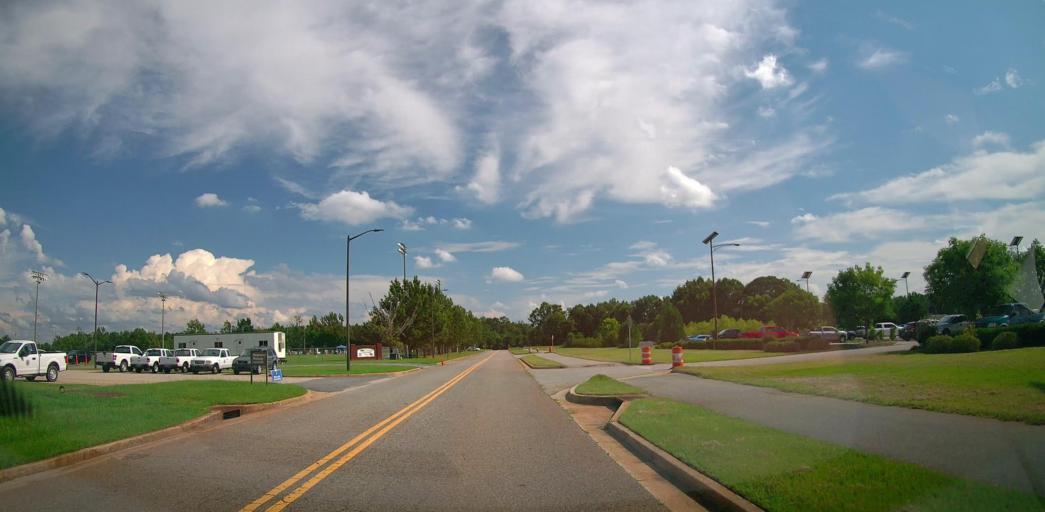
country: US
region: Georgia
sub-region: Houston County
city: Centerville
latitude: 32.5455
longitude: -83.6769
